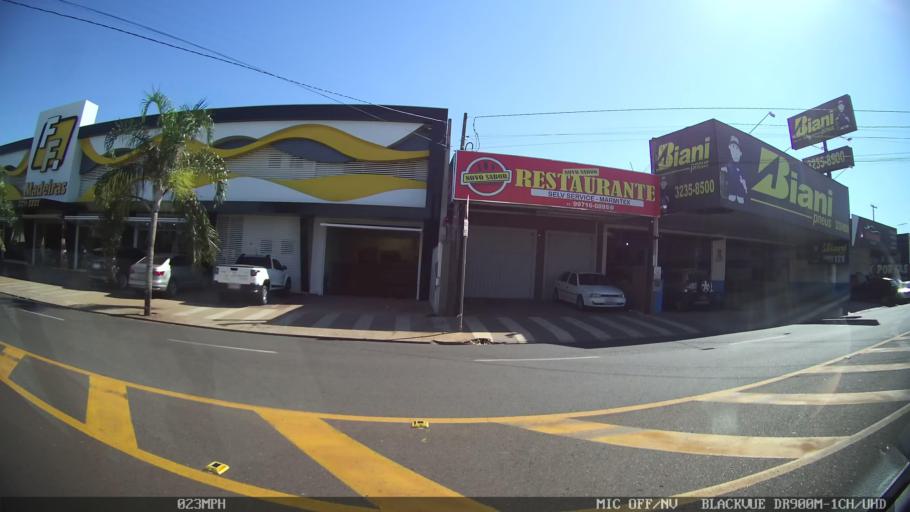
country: BR
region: Sao Paulo
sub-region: Sao Jose Do Rio Preto
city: Sao Jose do Rio Preto
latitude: -20.7967
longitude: -49.3922
